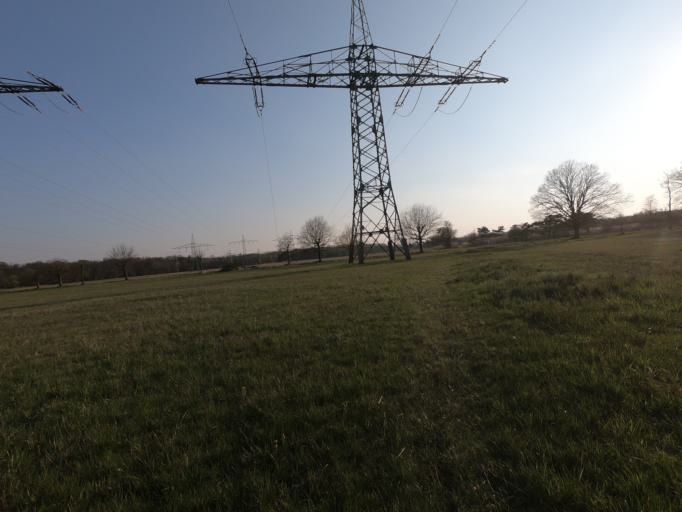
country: DE
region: Hesse
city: Morfelden-Walldorf
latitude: 49.9920
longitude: 8.5326
